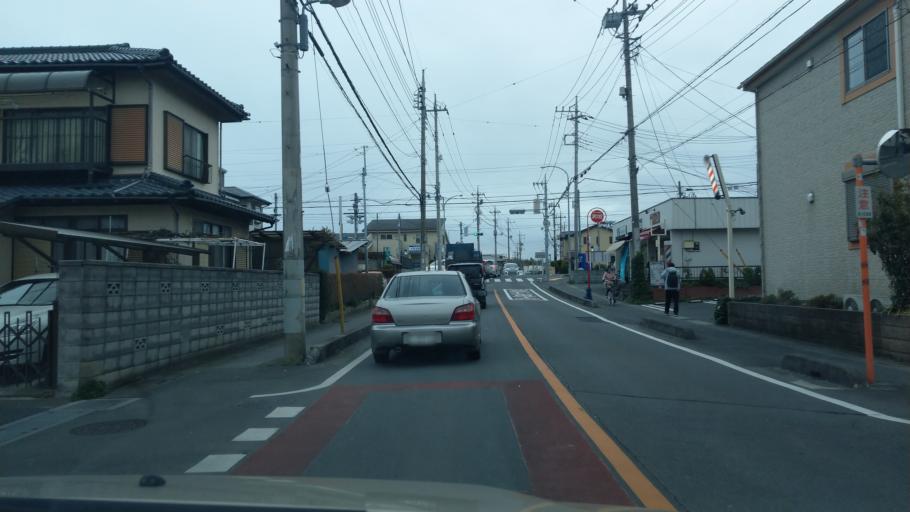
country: JP
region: Saitama
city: Saitama
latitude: 35.9255
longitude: 139.6463
